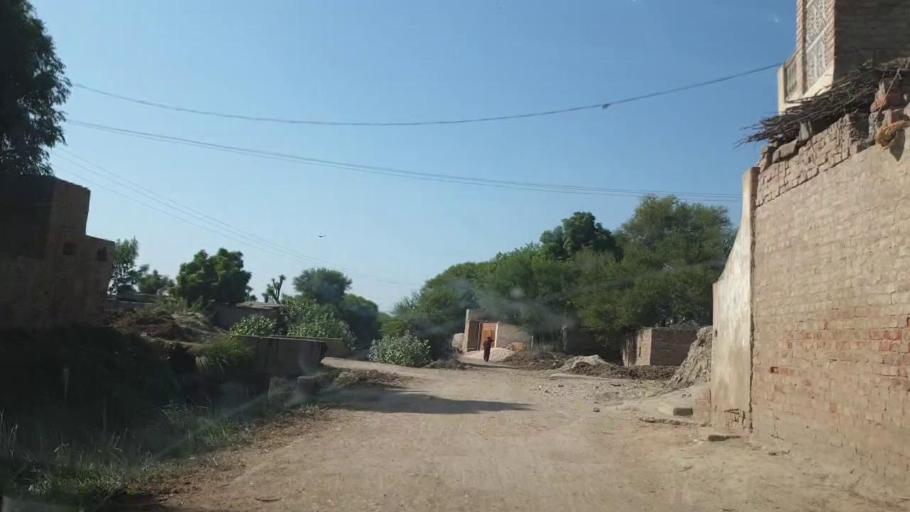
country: PK
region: Sindh
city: Tando Jam
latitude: 25.3143
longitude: 68.6075
